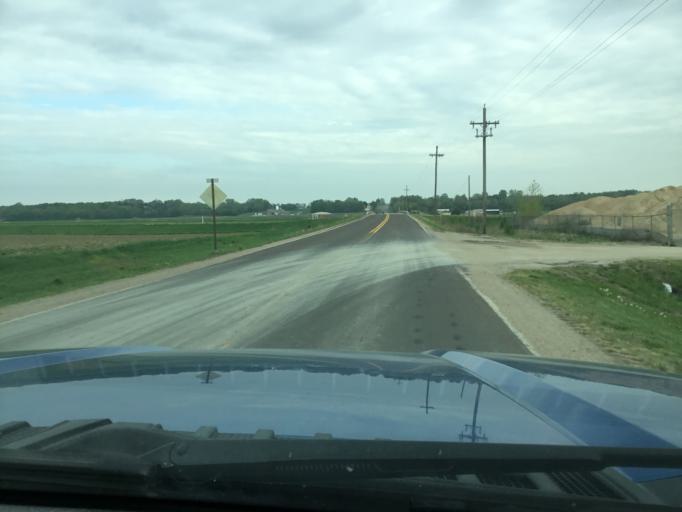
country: US
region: Kansas
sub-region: Shawnee County
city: Topeka
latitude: 39.0961
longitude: -95.7484
